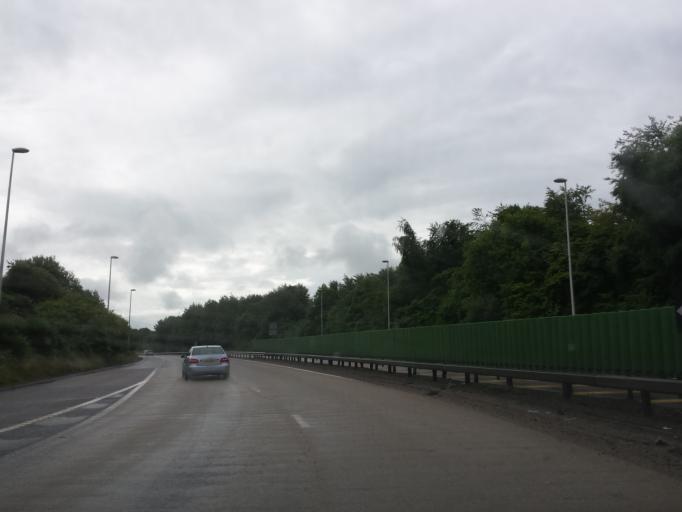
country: GB
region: Scotland
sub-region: Perth and Kinross
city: Perth
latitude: 56.3875
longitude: -3.4856
